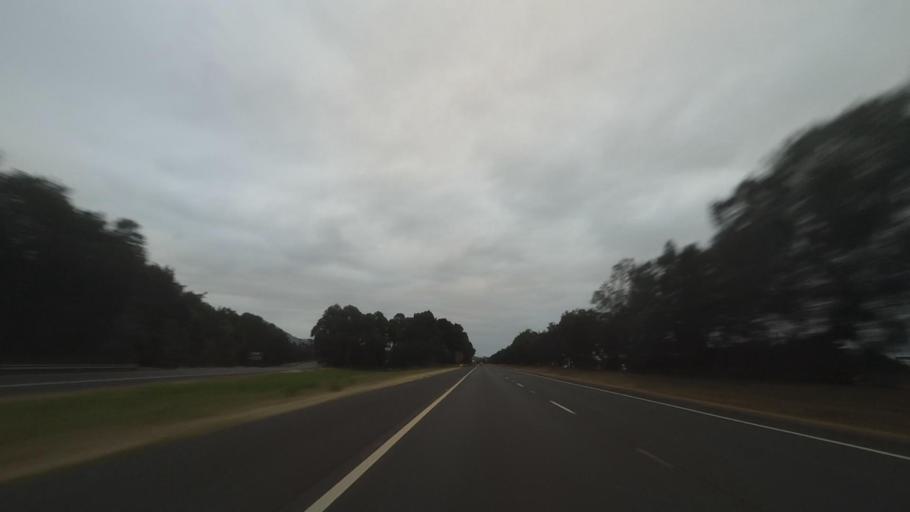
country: AU
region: New South Wales
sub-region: Wollongong
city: Mount Saint Thomas
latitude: -34.4591
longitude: 150.8543
